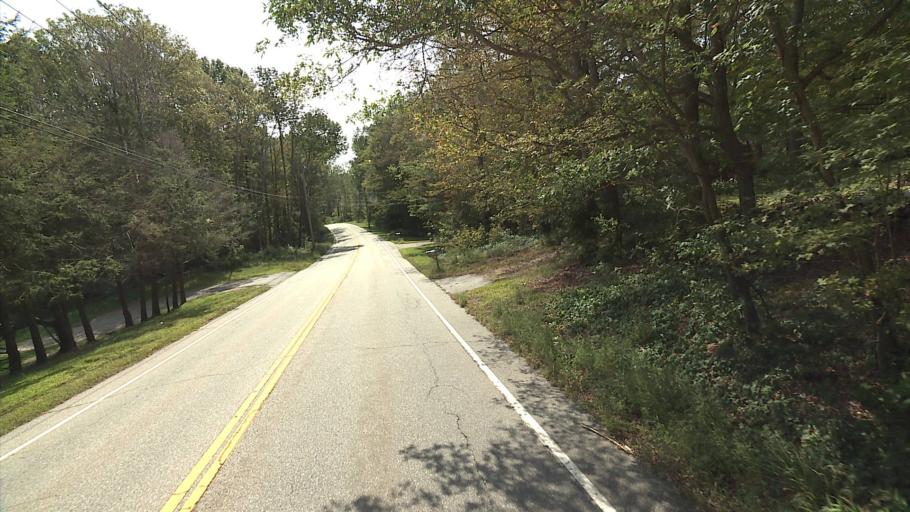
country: US
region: Connecticut
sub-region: Windham County
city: East Brooklyn
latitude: 41.8104
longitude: -71.9549
